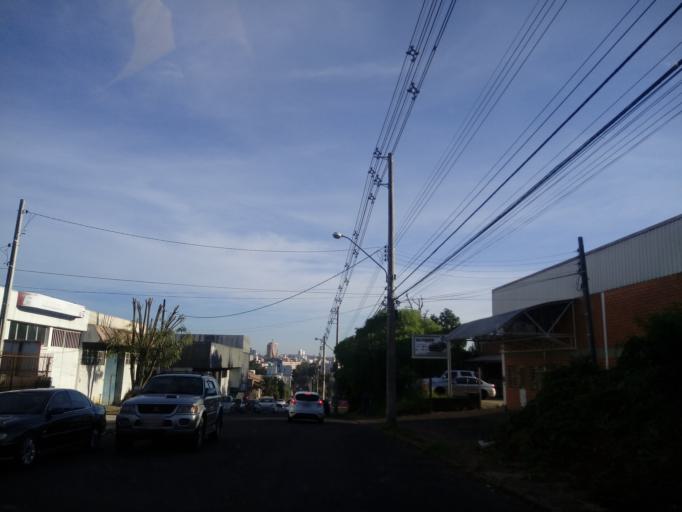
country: BR
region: Santa Catarina
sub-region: Chapeco
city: Chapeco
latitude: -27.1026
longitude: -52.6214
